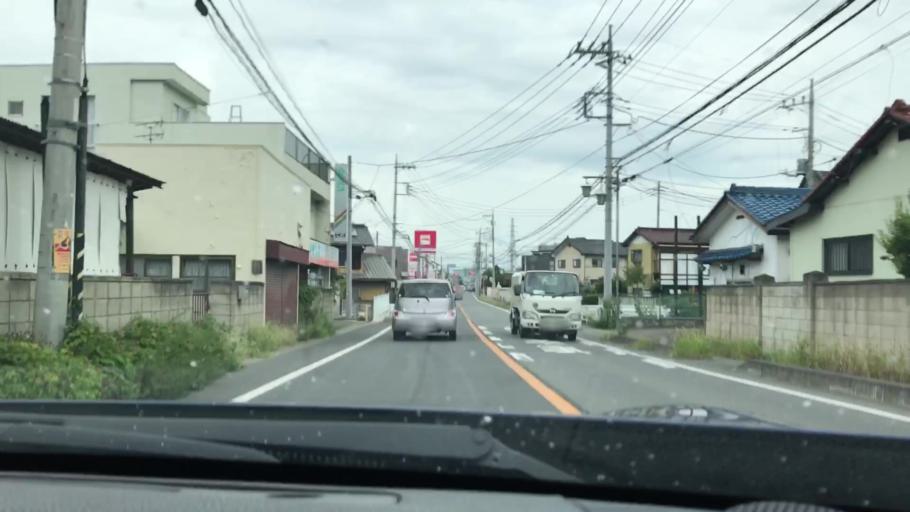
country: JP
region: Gunma
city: Takasaki
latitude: 36.3519
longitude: 139.0245
